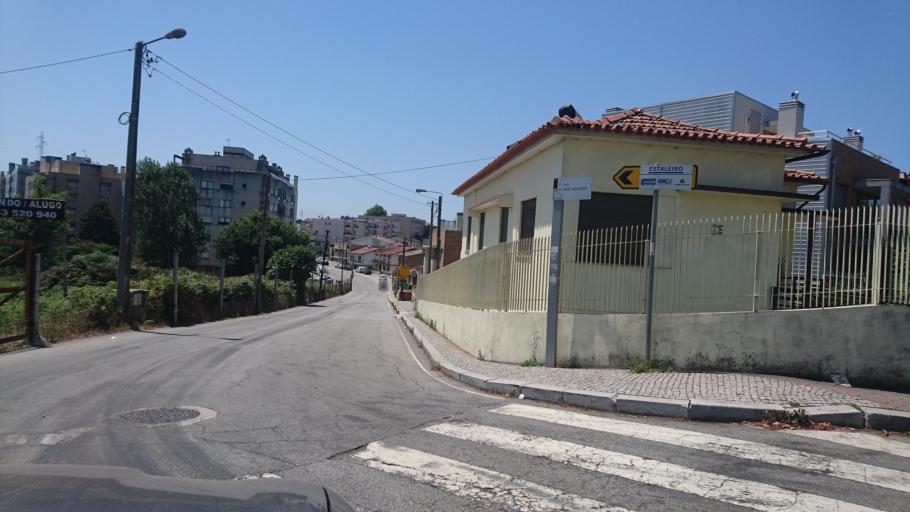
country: PT
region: Porto
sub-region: Valongo
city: Ermesinde
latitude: 41.2048
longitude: -8.5577
